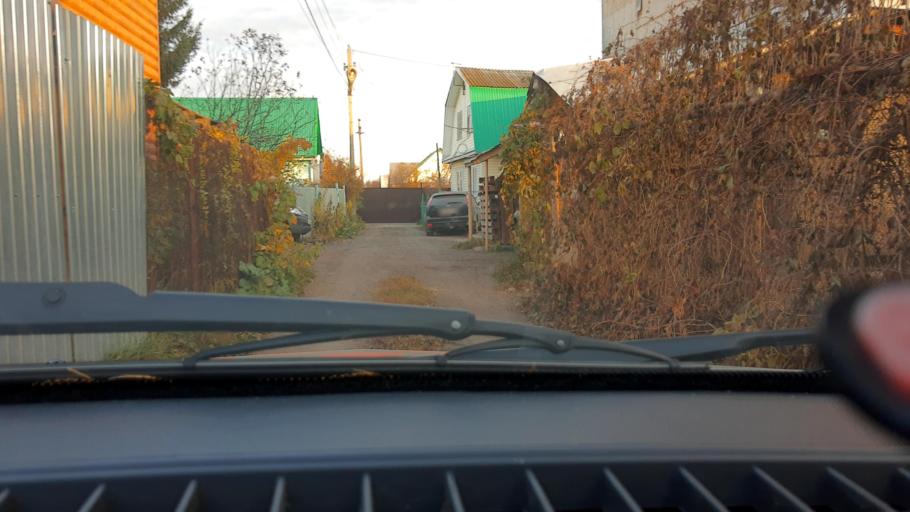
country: RU
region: Bashkortostan
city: Ufa
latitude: 54.6892
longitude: 55.9006
